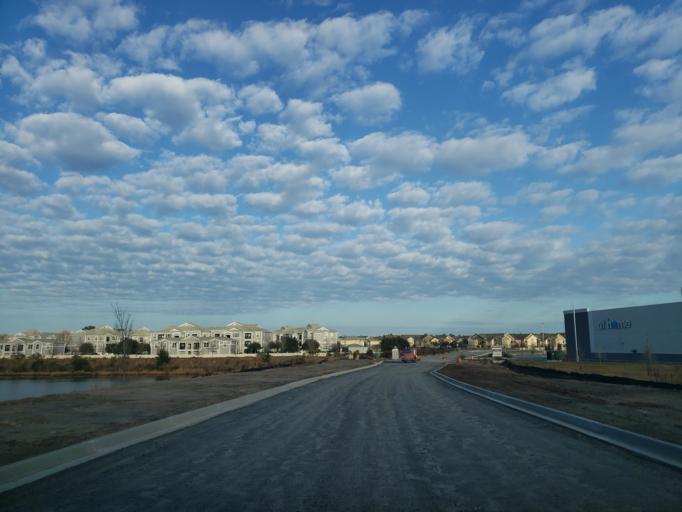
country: US
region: Georgia
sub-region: Chatham County
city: Pooler
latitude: 32.1297
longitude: -81.2474
